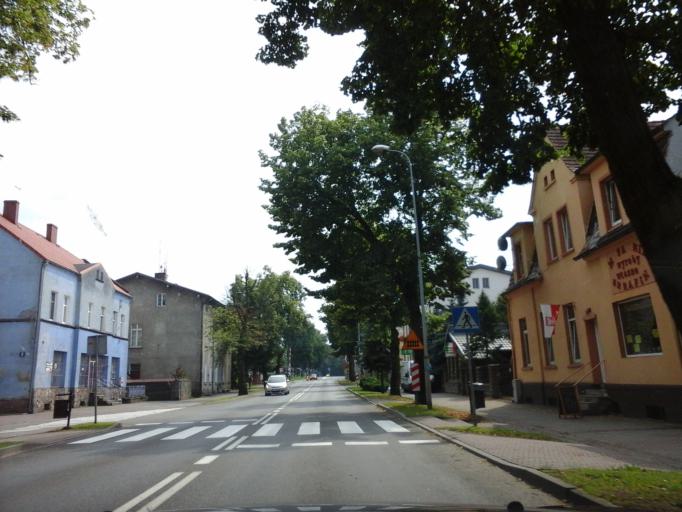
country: PL
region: Lubusz
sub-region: Powiat strzelecko-drezdenecki
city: Dobiegniew
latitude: 52.9683
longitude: 15.7511
